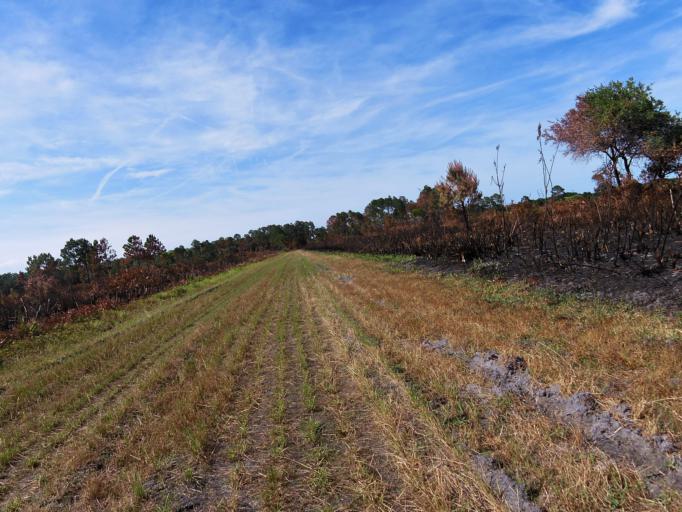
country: US
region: Florida
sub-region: Saint Johns County
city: Villano Beach
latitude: 30.0325
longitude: -81.3439
